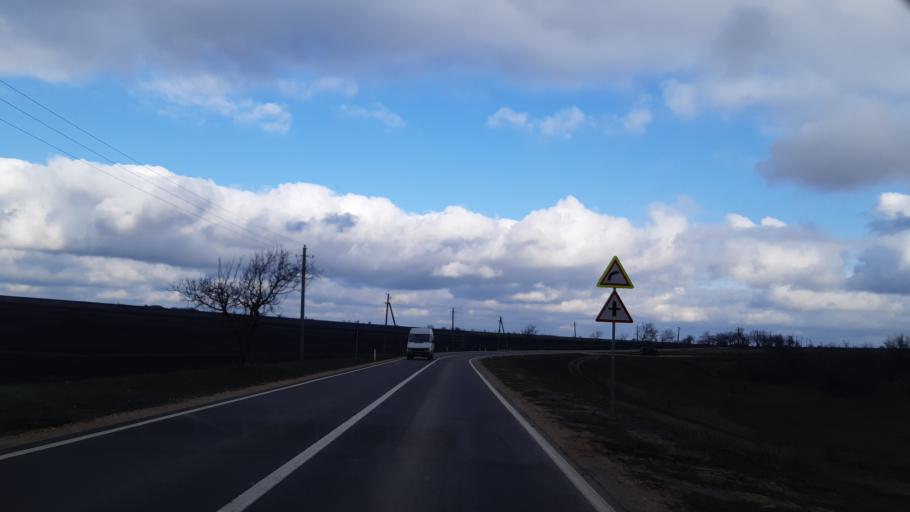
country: MD
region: Chisinau
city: Ciorescu
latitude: 47.2345
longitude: 28.9761
